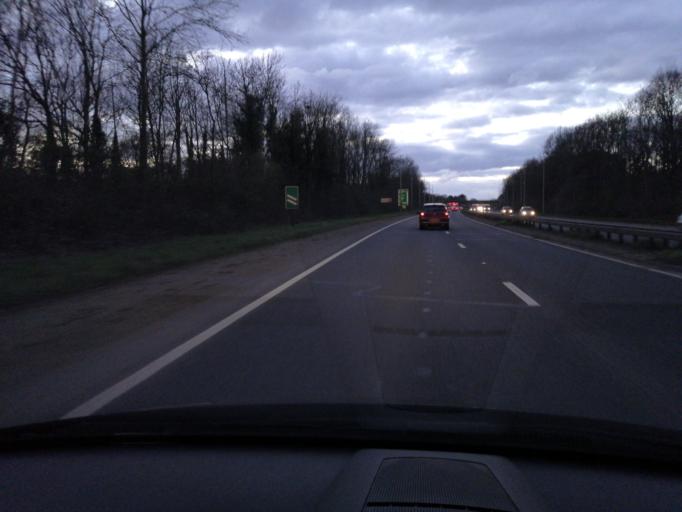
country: GB
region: England
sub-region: Peterborough
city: Eye
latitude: 52.6001
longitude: -0.2210
